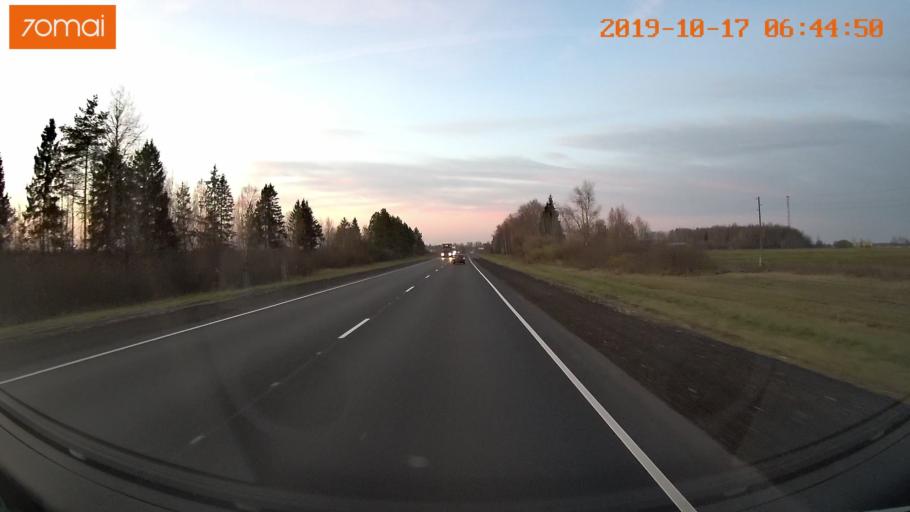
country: RU
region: Vladimir
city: Kideksha
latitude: 56.5668
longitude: 40.5519
